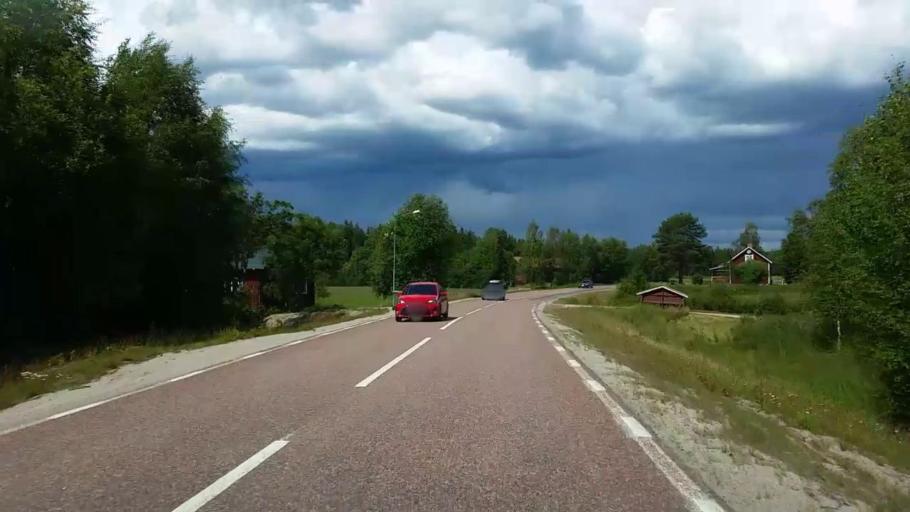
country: SE
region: Gaevleborg
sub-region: Ovanakers Kommun
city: Edsbyn
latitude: 61.3372
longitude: 15.5426
